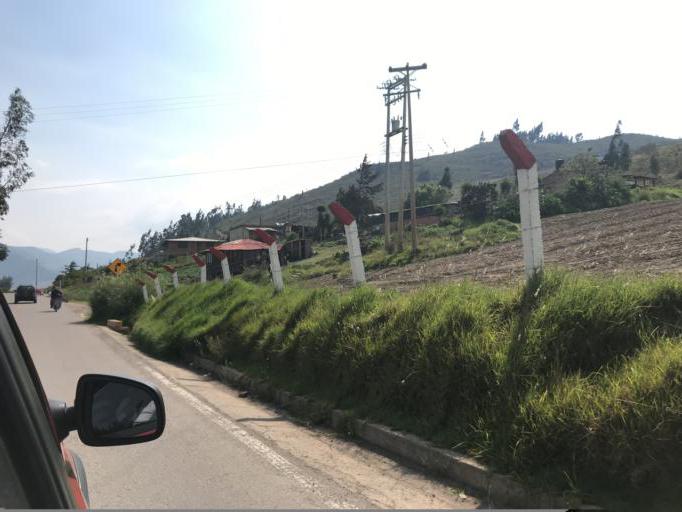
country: CO
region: Boyaca
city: Cucaita
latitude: 5.5468
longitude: -73.4915
